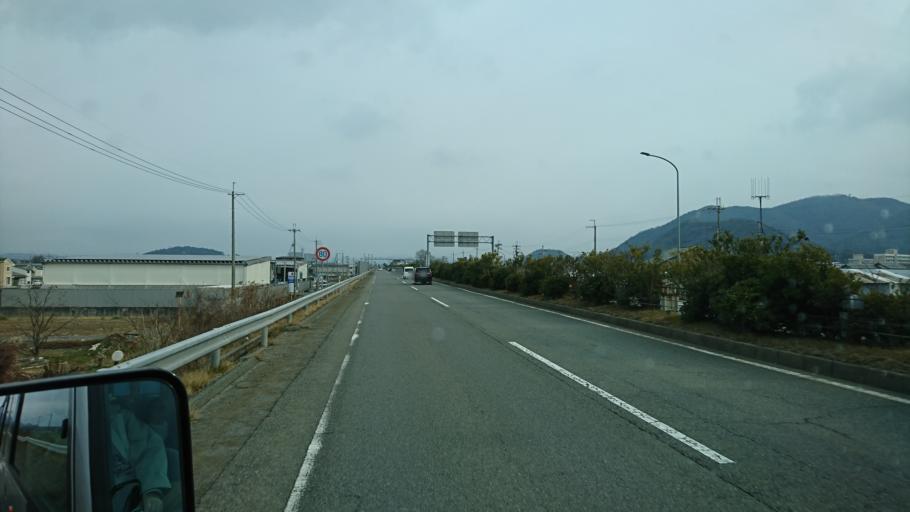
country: JP
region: Hyogo
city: Himeji
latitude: 34.8798
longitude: 134.7404
